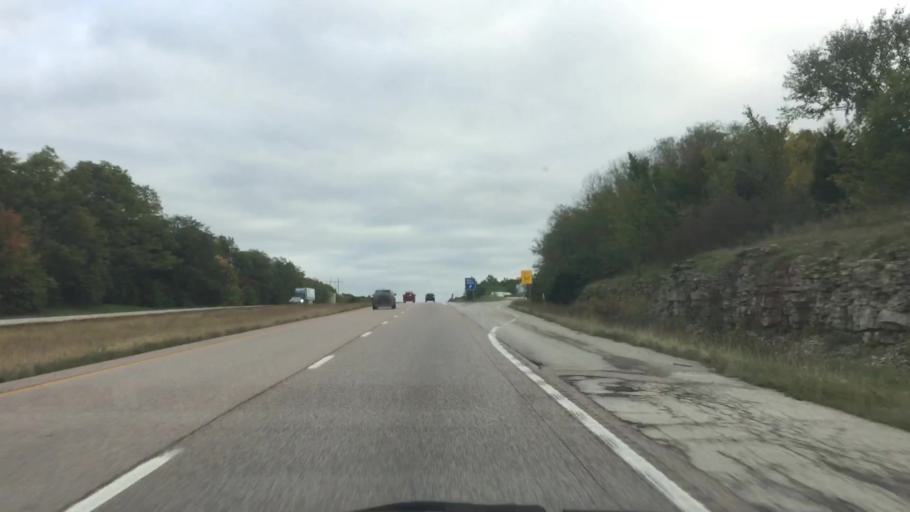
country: US
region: Missouri
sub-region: Clinton County
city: Lathrop
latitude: 39.4723
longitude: -94.3128
